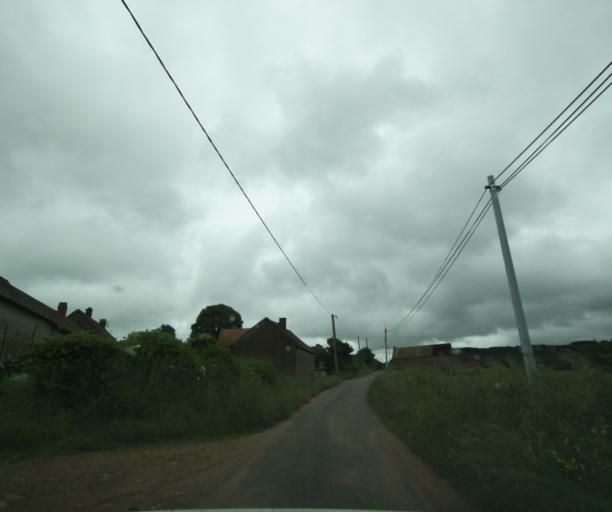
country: FR
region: Bourgogne
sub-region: Departement de Saone-et-Loire
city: Matour
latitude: 46.4564
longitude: 4.4567
